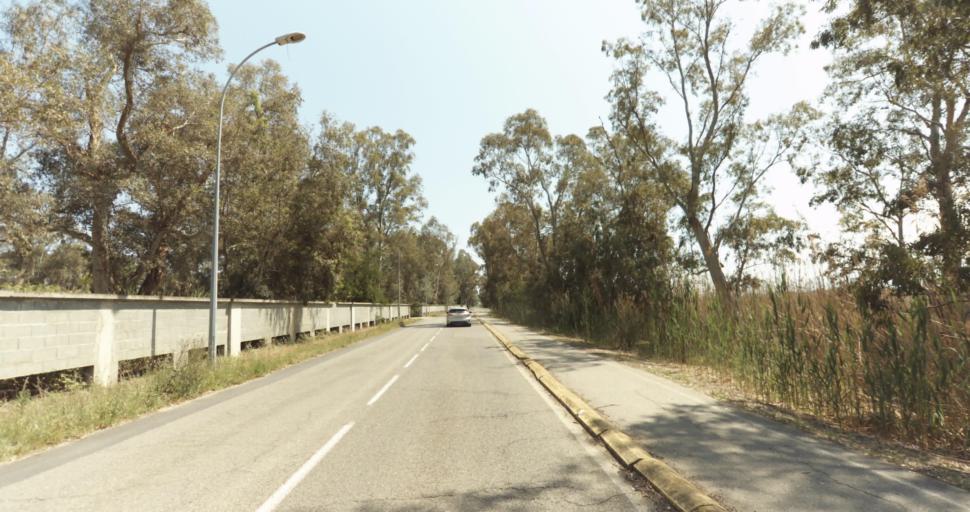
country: FR
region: Corsica
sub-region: Departement de la Haute-Corse
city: Biguglia
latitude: 42.6138
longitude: 9.4799
